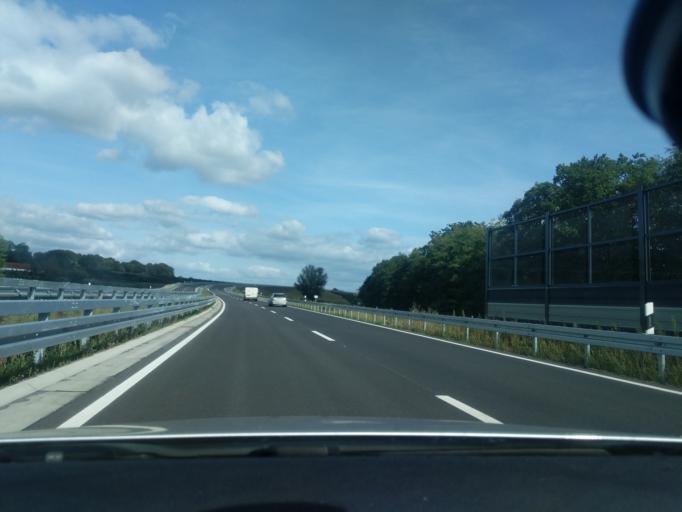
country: DE
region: Lower Saxony
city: Belm
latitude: 52.3177
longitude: 8.1375
